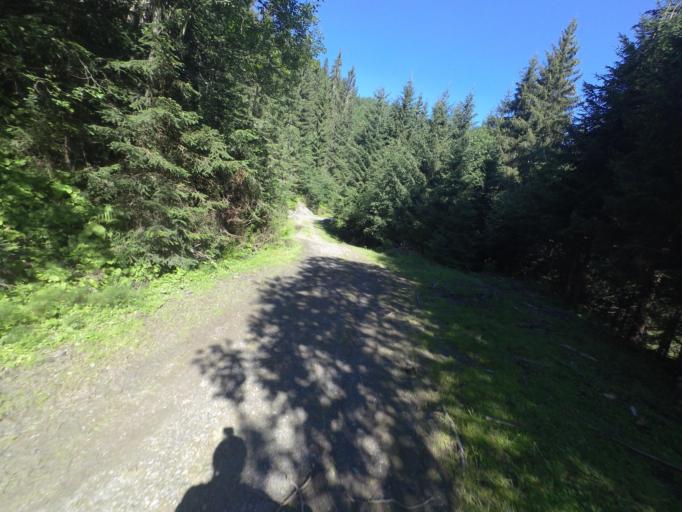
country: AT
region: Salzburg
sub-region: Politischer Bezirk Sankt Johann im Pongau
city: Sankt Veit im Pongau
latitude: 47.3491
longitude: 13.1518
